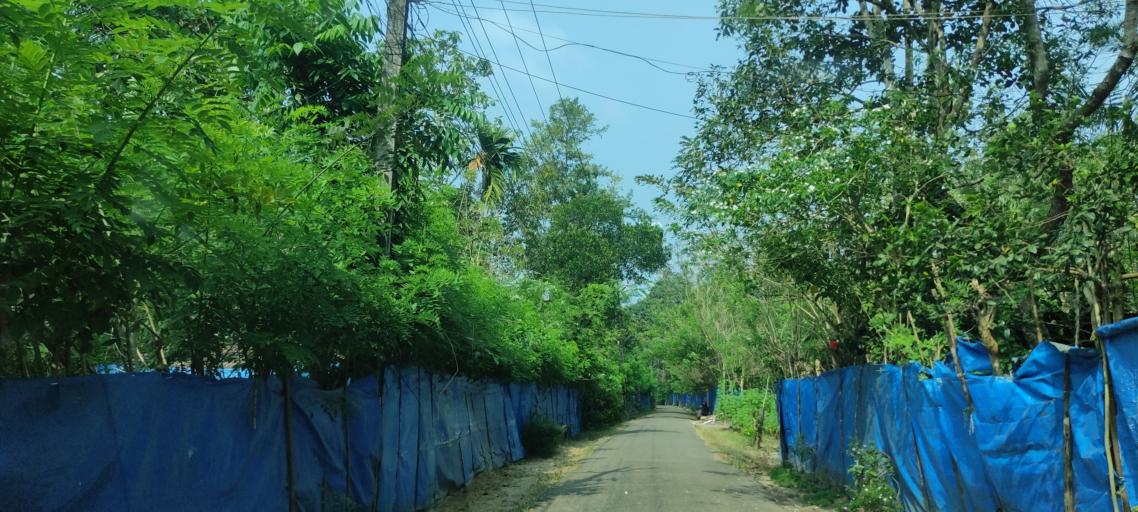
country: IN
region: Kerala
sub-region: Alappuzha
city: Shertallai
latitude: 9.6800
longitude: 76.3375
